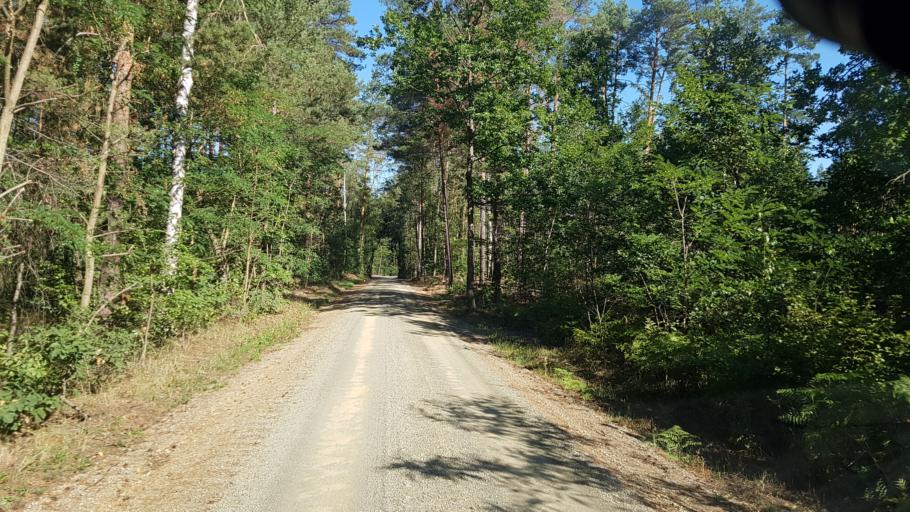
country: DE
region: Brandenburg
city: Ruckersdorf
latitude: 51.5435
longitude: 13.5806
